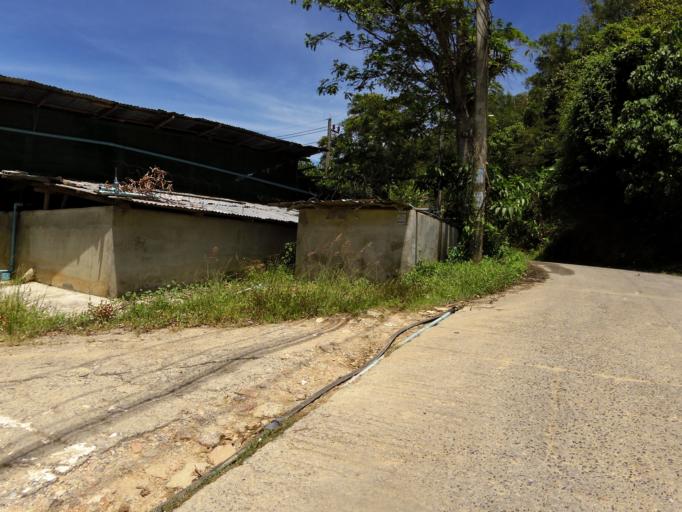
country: TH
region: Phuket
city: Ban Karon
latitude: 7.8498
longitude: 98.3036
